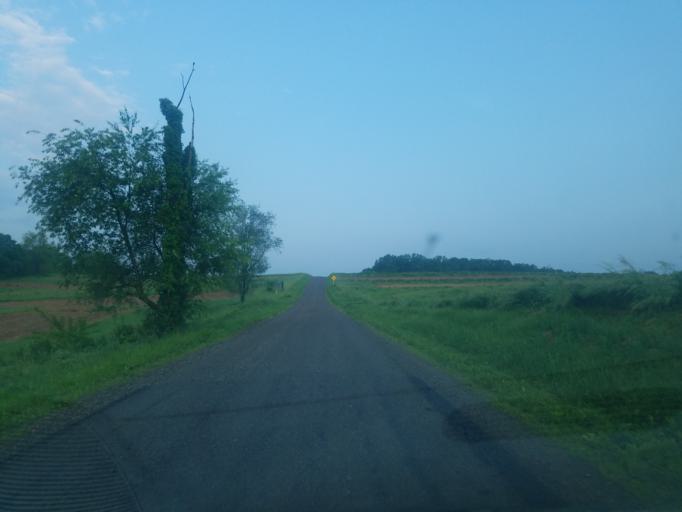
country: US
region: Ohio
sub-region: Stark County
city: Minerva
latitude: 40.7575
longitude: -80.9594
